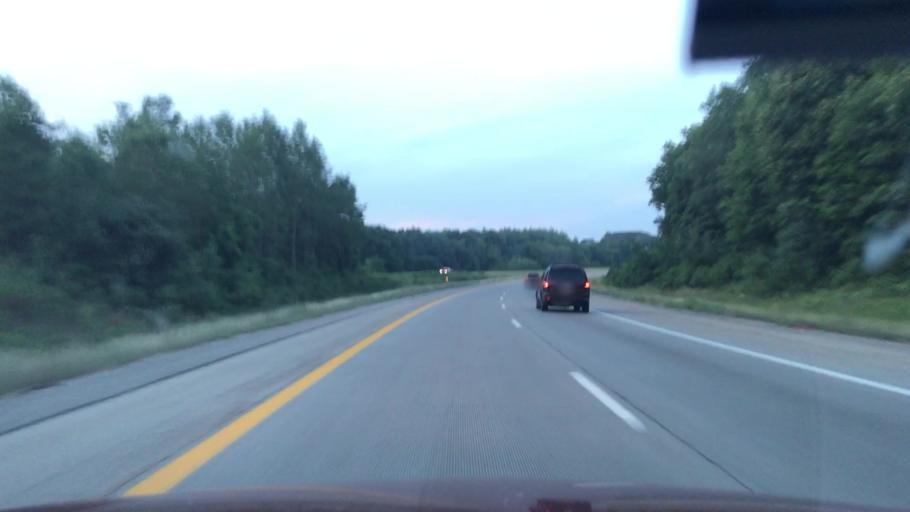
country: US
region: Michigan
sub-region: Kent County
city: Comstock Park
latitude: 43.0651
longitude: -85.6610
